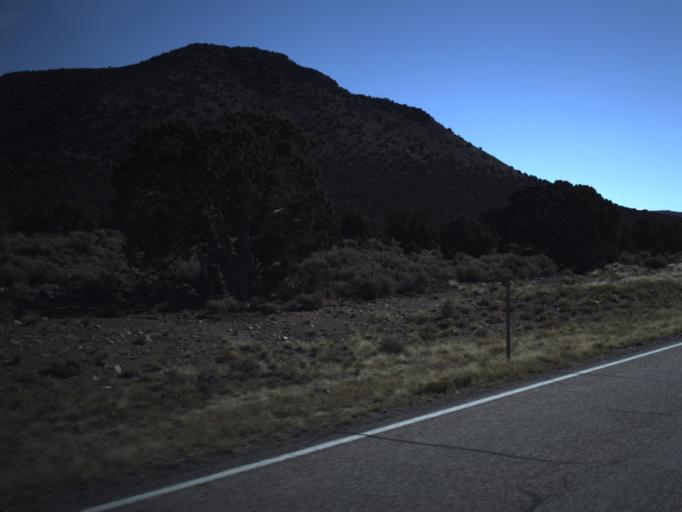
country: US
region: Utah
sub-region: Washington County
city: Enterprise
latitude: 37.6627
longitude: -113.4661
